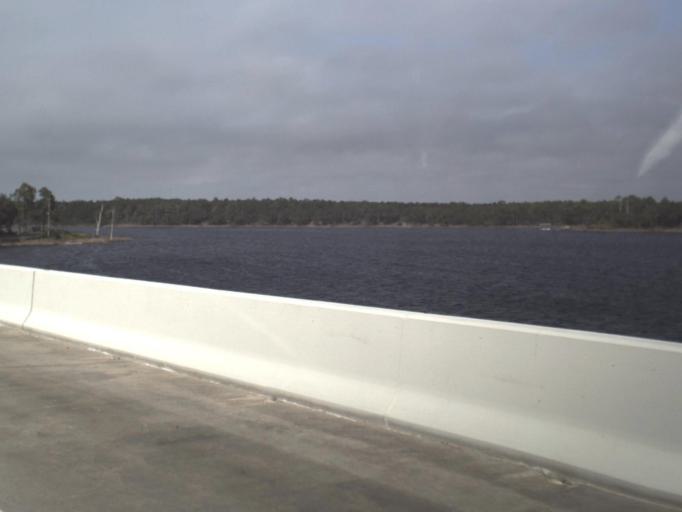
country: US
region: Florida
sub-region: Bay County
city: Laguna Beach
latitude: 30.2741
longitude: -85.9862
